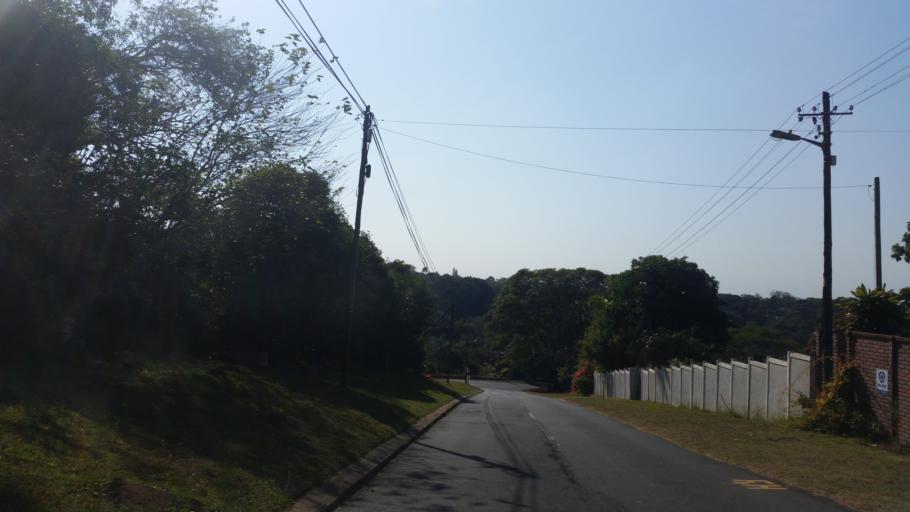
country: ZA
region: KwaZulu-Natal
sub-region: eThekwini Metropolitan Municipality
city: Berea
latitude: -29.8471
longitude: 30.9011
